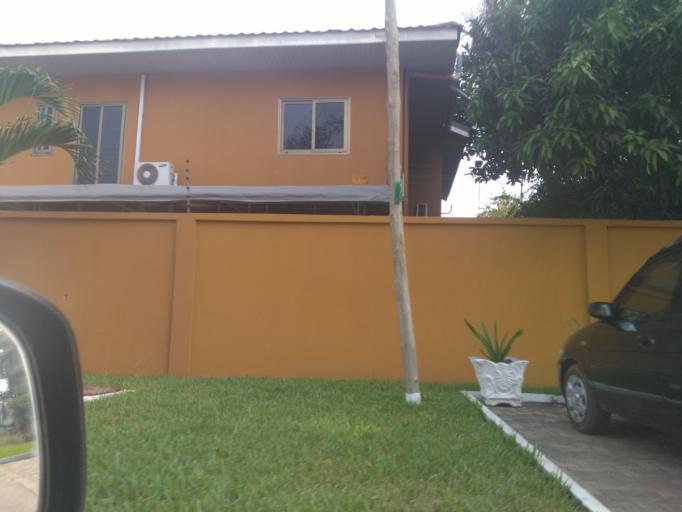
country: GH
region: Greater Accra
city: Accra
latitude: 5.6060
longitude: -0.2015
